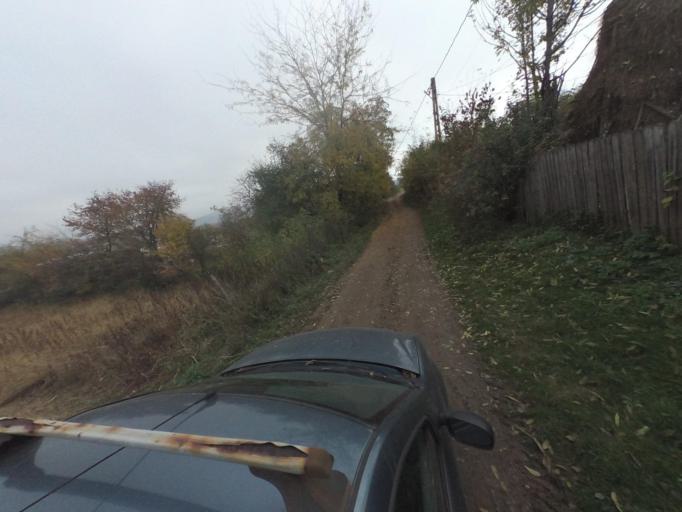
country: RO
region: Vaslui
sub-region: Comuna Bacesti
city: Bacesti
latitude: 46.8333
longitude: 27.2304
